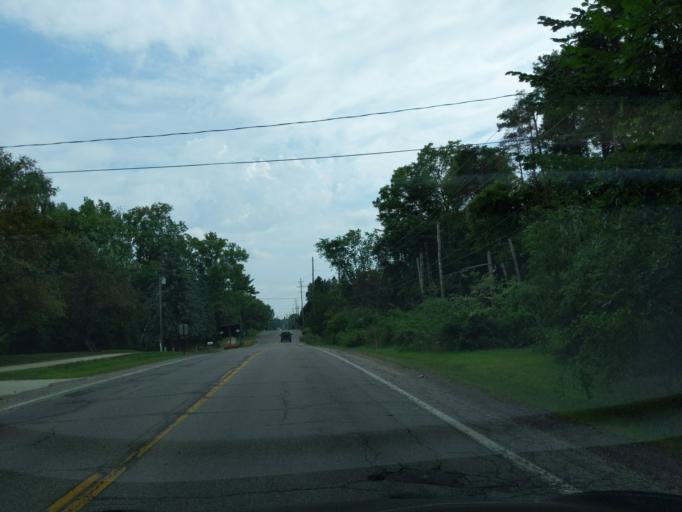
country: US
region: Michigan
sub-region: Ingham County
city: Okemos
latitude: 42.7292
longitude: -84.4276
